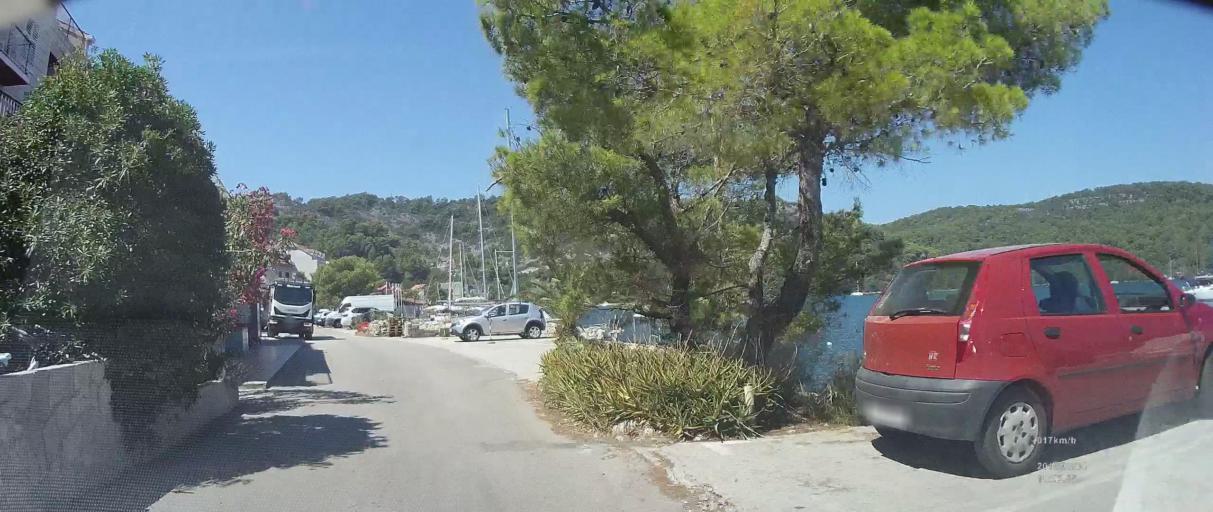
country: HR
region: Dubrovacko-Neretvanska
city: Blato
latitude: 42.7874
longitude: 17.3824
